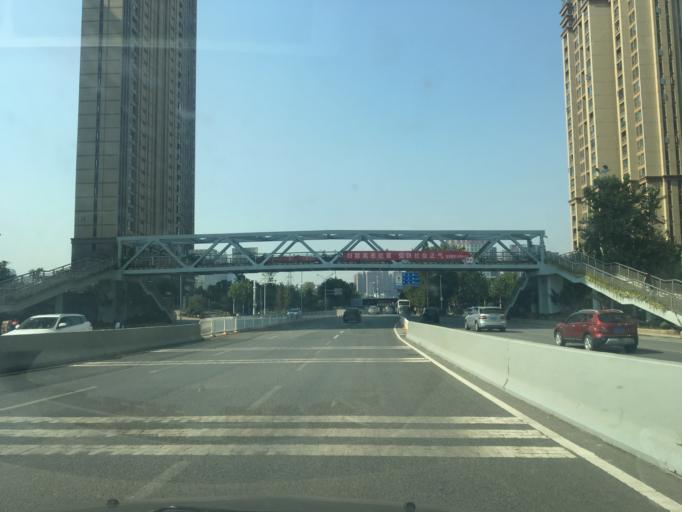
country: CN
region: Hubei
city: Jiang'an
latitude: 30.5712
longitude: 114.3150
